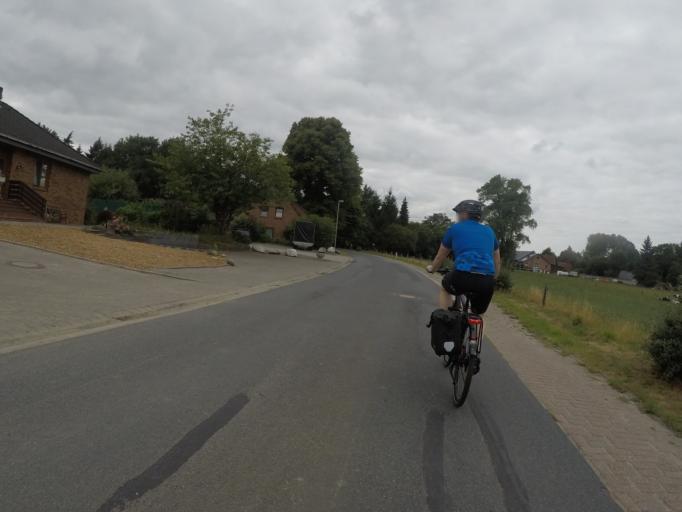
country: DE
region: Lower Saxony
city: Hemmoor
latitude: 53.6965
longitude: 9.1183
